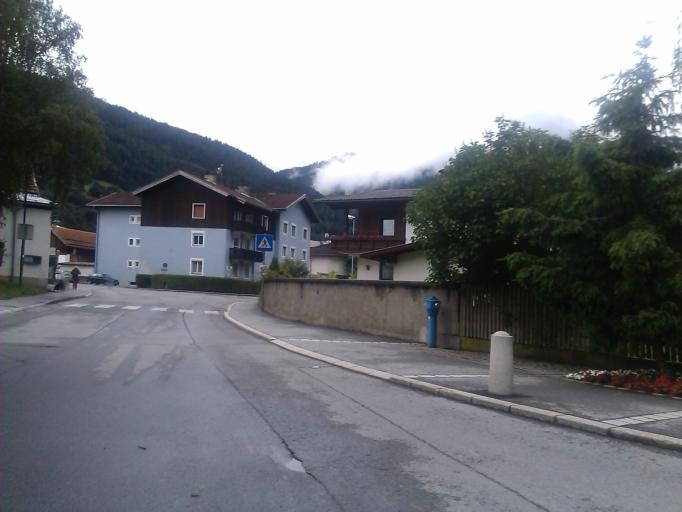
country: AT
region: Tyrol
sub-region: Politischer Bezirk Landeck
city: Landeck
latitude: 47.1503
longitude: 10.5698
